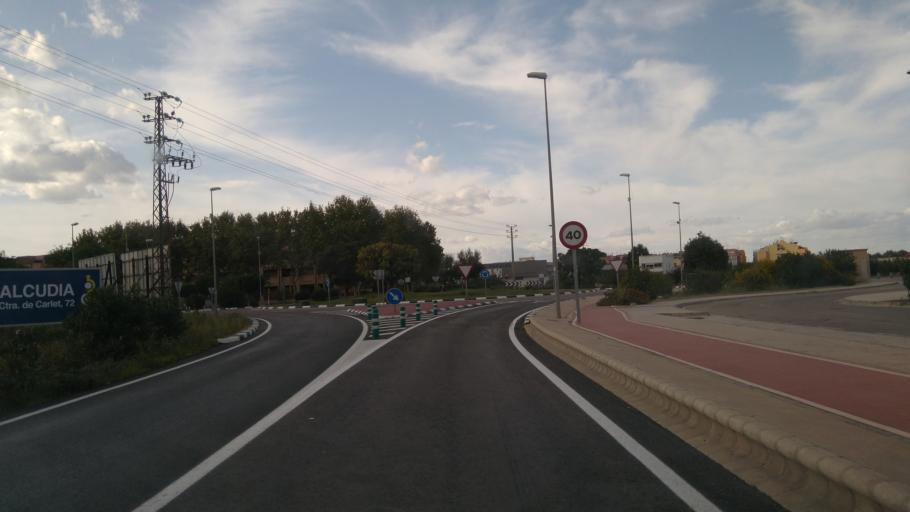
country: ES
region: Valencia
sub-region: Provincia de Valencia
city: L'Alcudia
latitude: 39.1954
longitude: -0.4982
